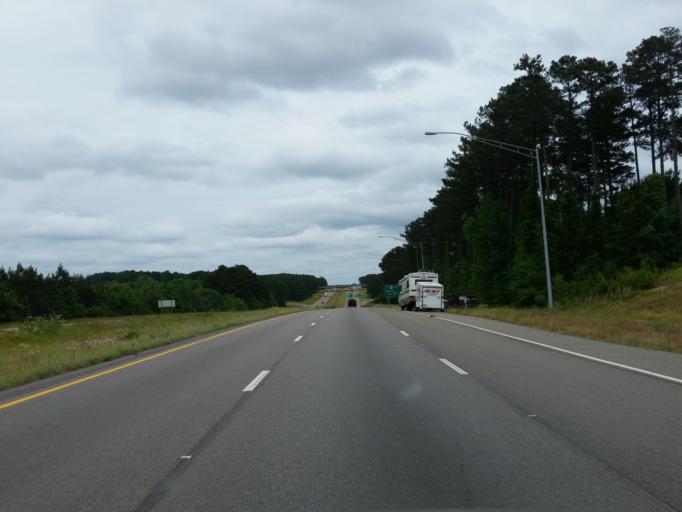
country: US
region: Mississippi
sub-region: Lauderdale County
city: Marion
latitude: 32.3810
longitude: -88.6480
